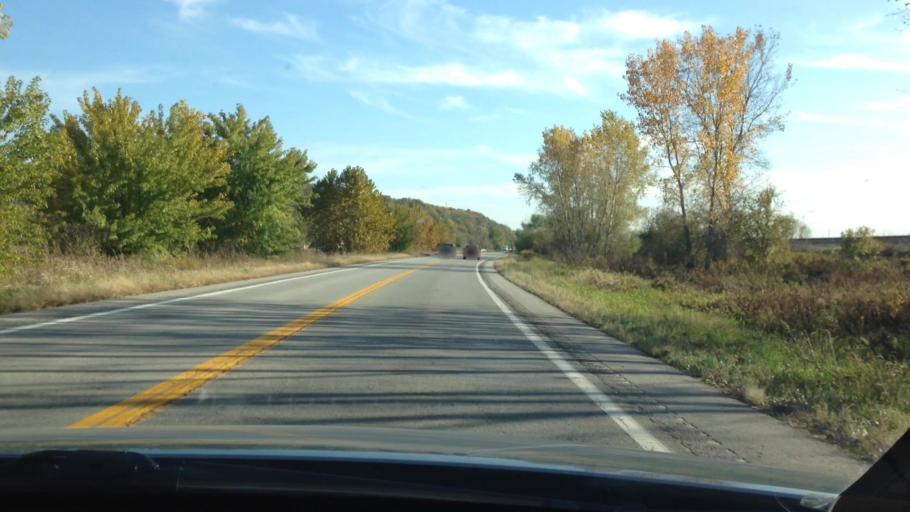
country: US
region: Kansas
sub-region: Leavenworth County
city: Lansing
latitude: 39.2561
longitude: -94.8080
